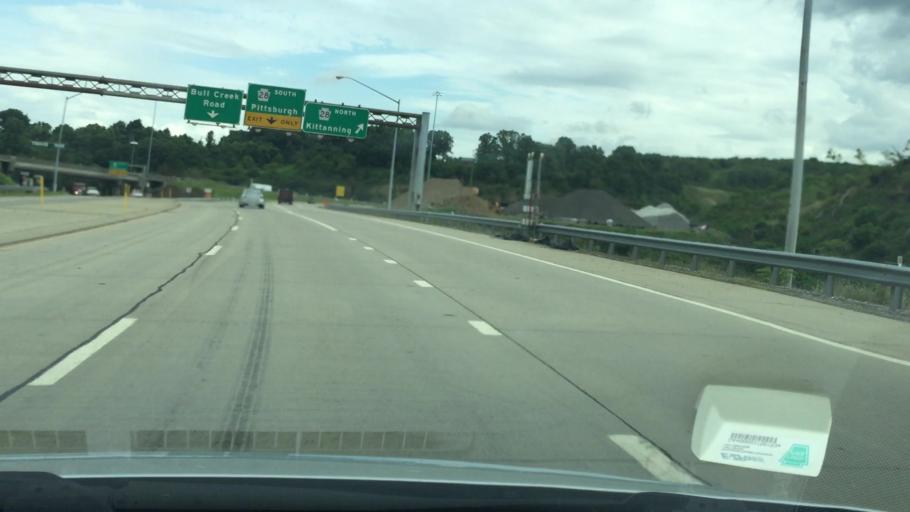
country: US
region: Pennsylvania
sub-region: Allegheny County
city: Tarentum
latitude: 40.6113
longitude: -79.7565
